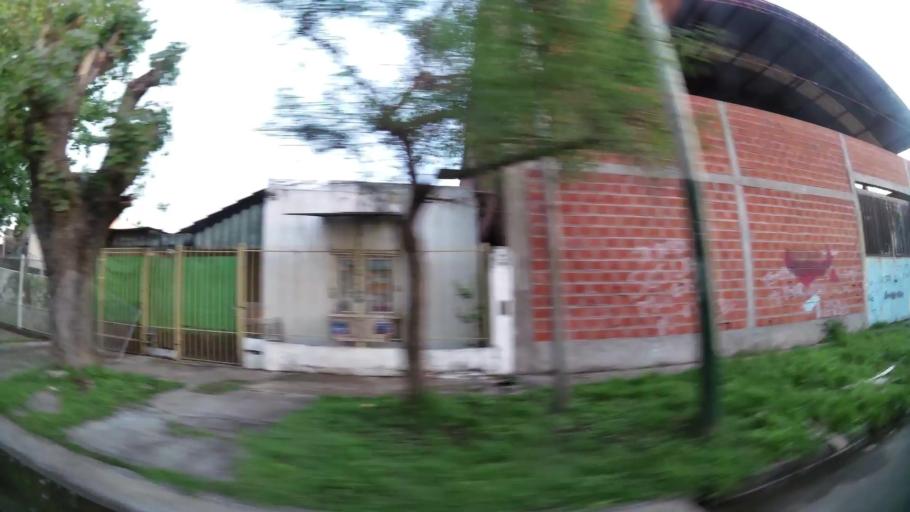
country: AR
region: Buenos Aires
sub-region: Partido de Lomas de Zamora
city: Lomas de Zamora
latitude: -34.7666
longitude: -58.3758
